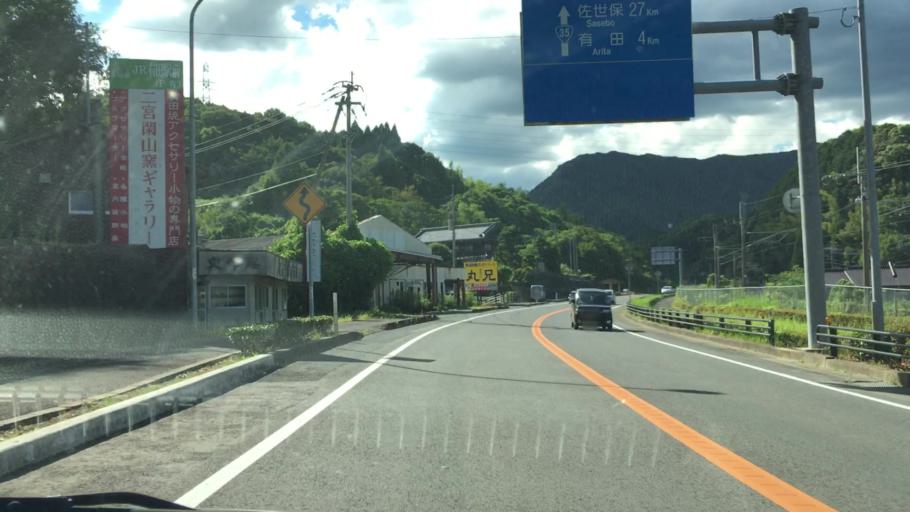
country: JP
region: Saga Prefecture
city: Takeocho-takeo
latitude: 33.1886
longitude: 129.9246
